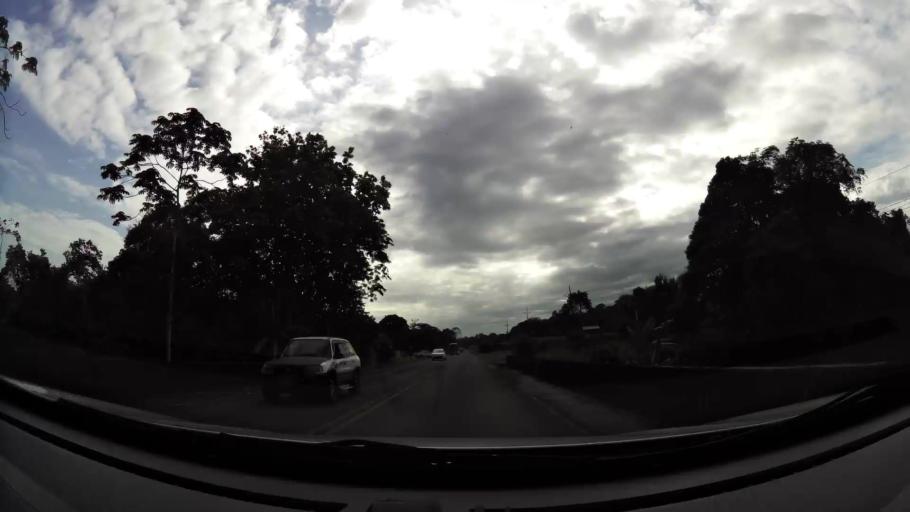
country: CR
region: Limon
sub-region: Canton de Guacimo
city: Guacimo
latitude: 10.2043
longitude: -83.6815
